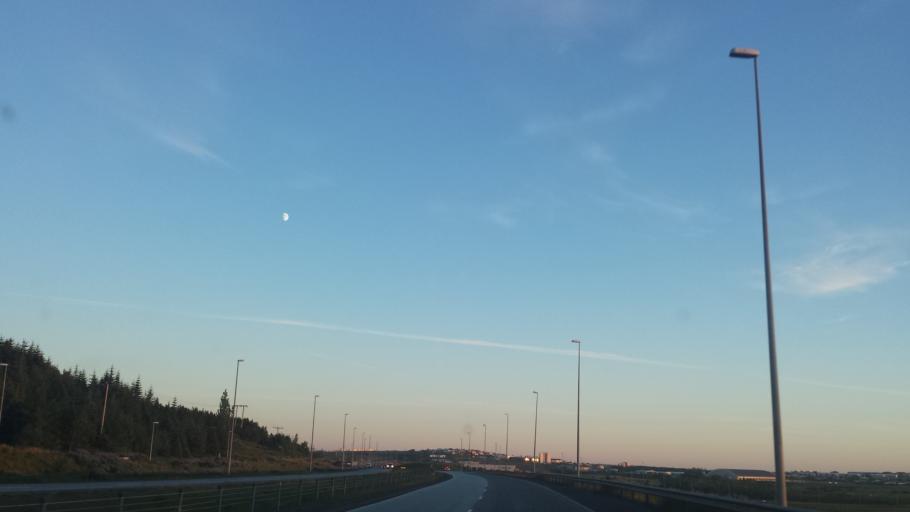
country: IS
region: Capital Region
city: Mosfellsbaer
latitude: 64.1561
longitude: -21.7323
